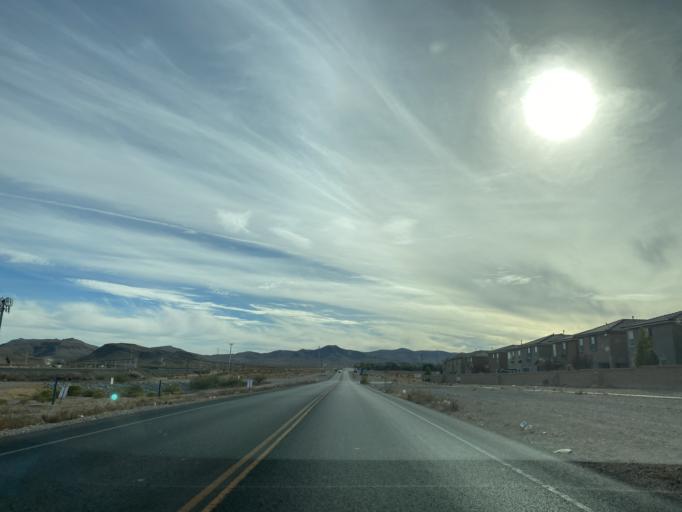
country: US
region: Nevada
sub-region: Clark County
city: Enterprise
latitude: 35.9969
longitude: -115.2435
